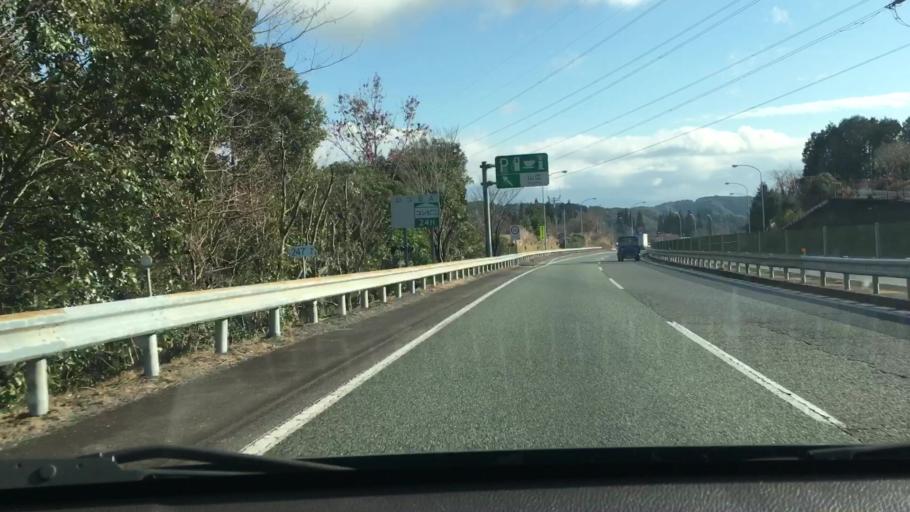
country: JP
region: Kumamoto
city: Hitoyoshi
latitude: 32.2646
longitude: 130.7664
